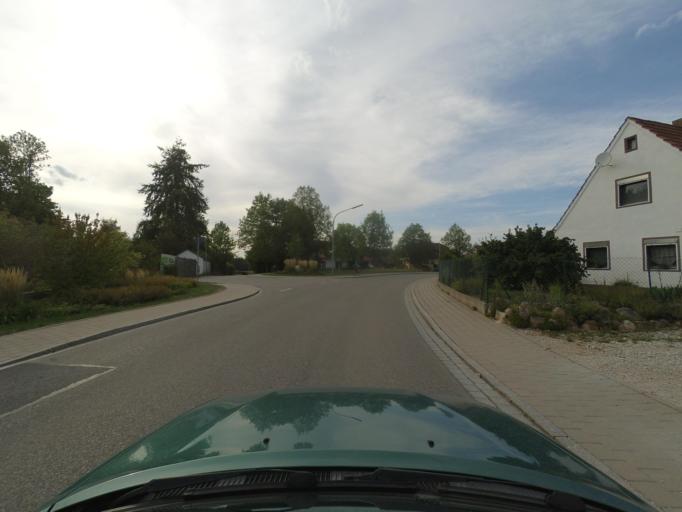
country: DE
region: Bavaria
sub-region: Upper Palatinate
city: Pyrbaum
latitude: 49.2752
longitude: 11.3000
